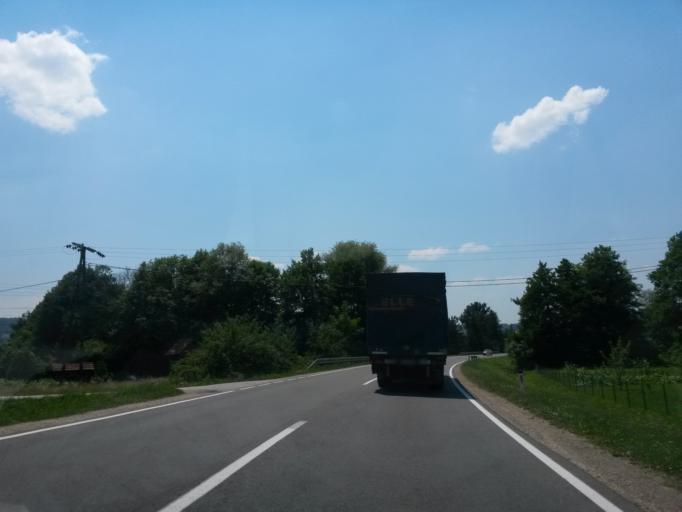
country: BA
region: Federation of Bosnia and Herzegovina
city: Lijesnica
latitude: 44.4896
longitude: 18.0844
